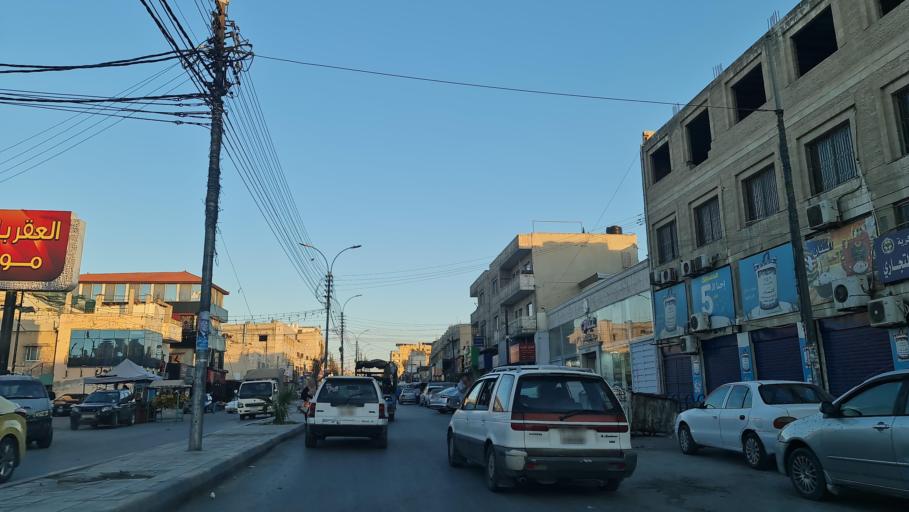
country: JO
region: Zarqa
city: Zarqa
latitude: 32.0772
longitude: 36.0759
